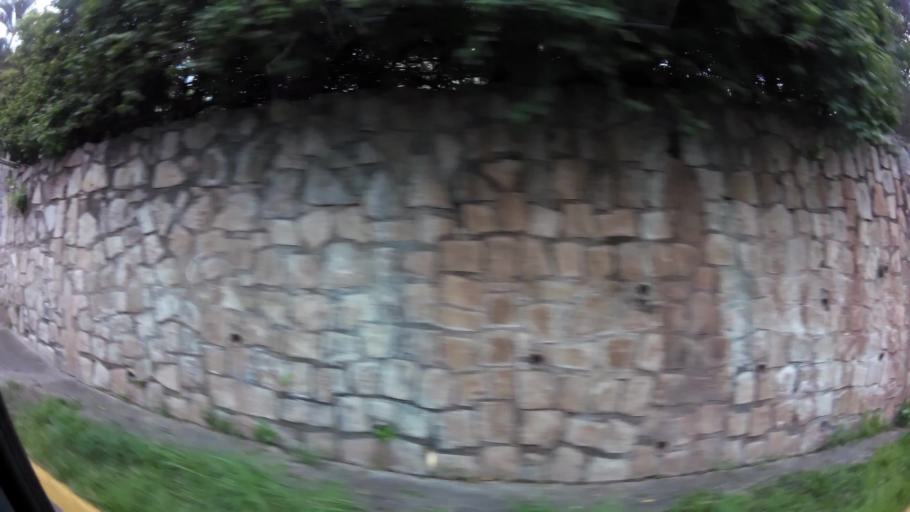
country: HN
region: Francisco Morazan
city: Tegucigalpa
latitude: 14.0968
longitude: -87.1790
